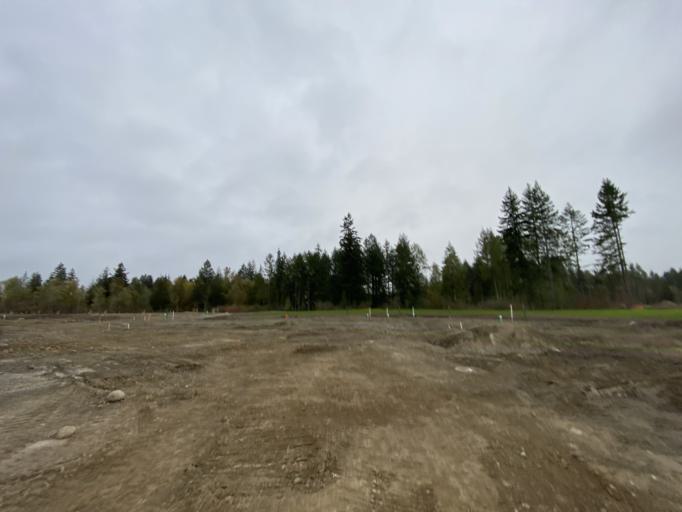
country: US
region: Washington
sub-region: Pierce County
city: South Hill
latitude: 47.0946
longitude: -122.2579
